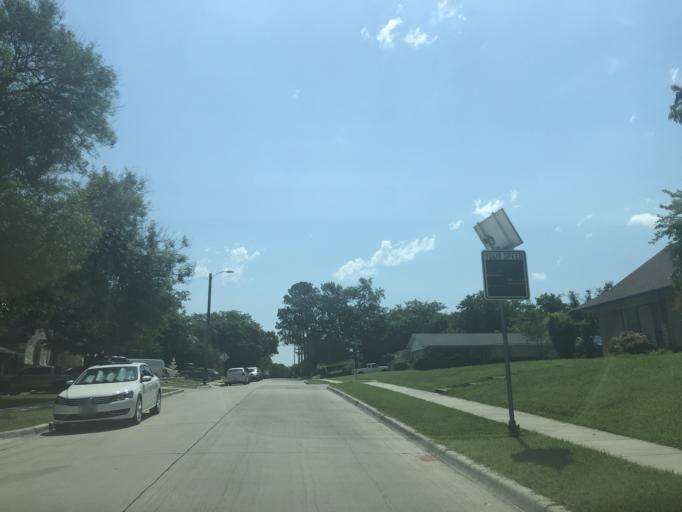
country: US
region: Texas
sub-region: Dallas County
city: Grand Prairie
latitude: 32.7243
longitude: -97.0039
